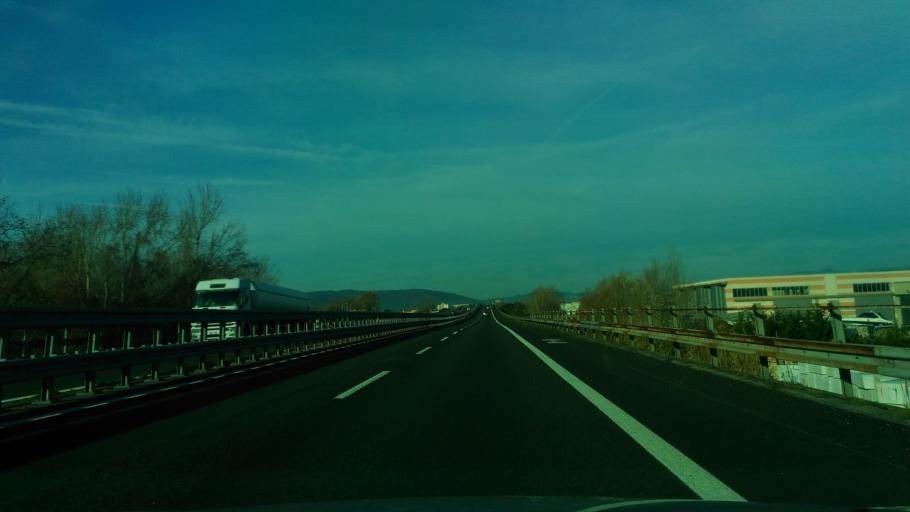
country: IT
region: Tuscany
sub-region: Provincia di Massa-Carrara
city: Carrara
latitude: 44.0355
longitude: 10.0694
